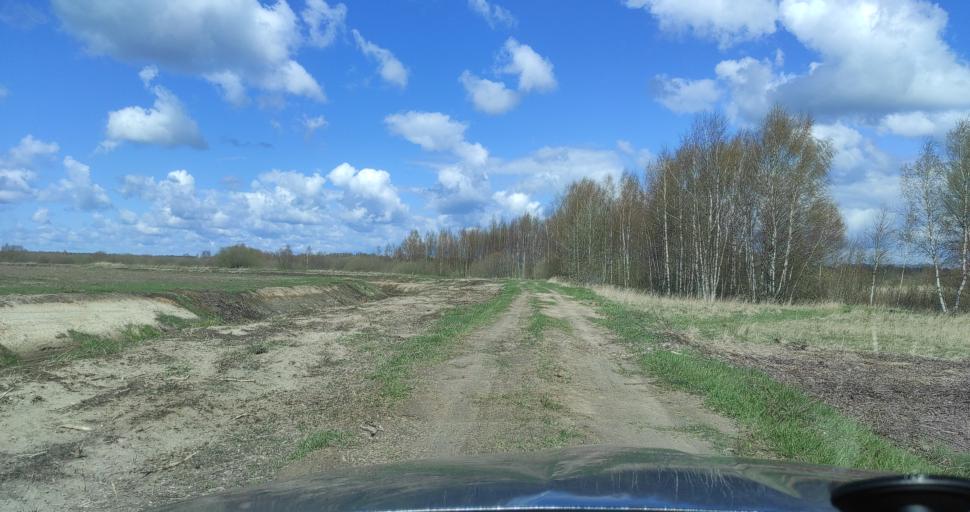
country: LV
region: Kuldigas Rajons
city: Kuldiga
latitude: 56.8725
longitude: 21.7891
